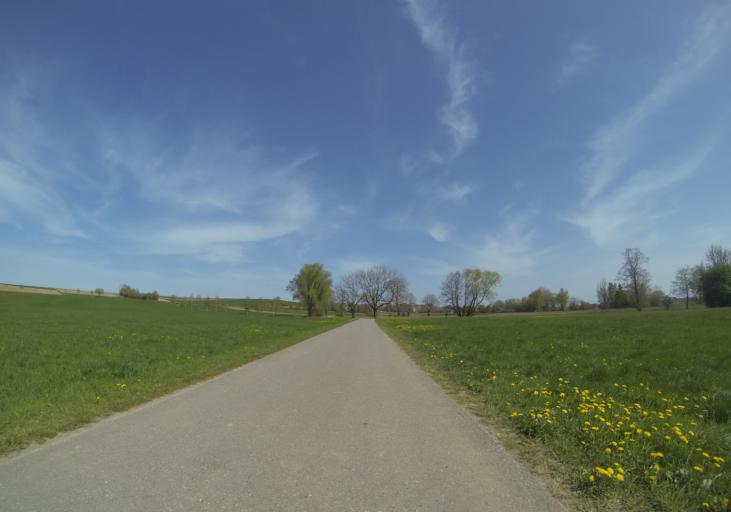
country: DE
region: Baden-Wuerttemberg
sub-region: Tuebingen Region
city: Achstetten
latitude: 48.2466
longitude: 9.9151
